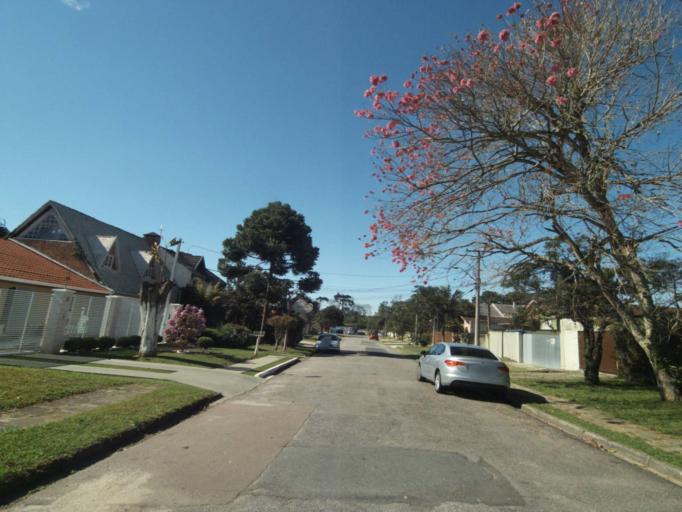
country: BR
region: Parana
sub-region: Curitiba
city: Curitiba
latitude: -25.4080
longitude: -49.2823
